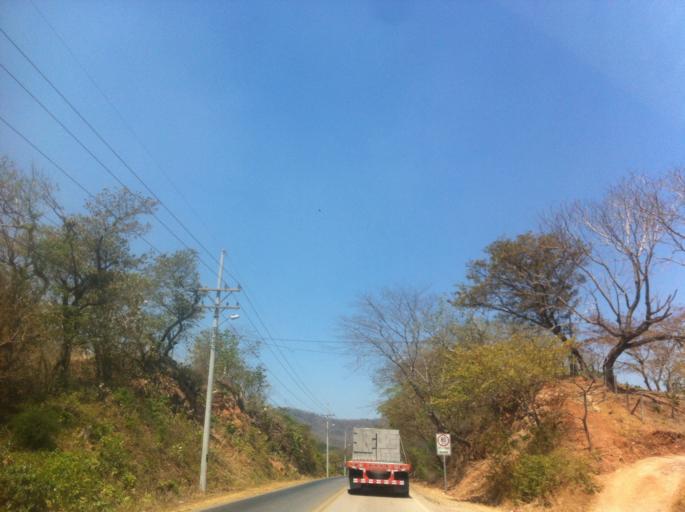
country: CR
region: Guanacaste
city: Santa Cruz
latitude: 10.2247
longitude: -85.5401
